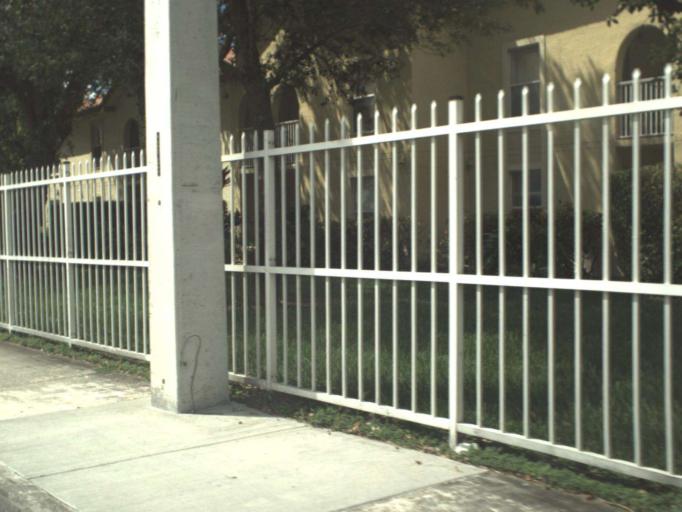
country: US
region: Florida
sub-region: Miami-Dade County
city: The Crossings
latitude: 25.6804
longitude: -80.4168
